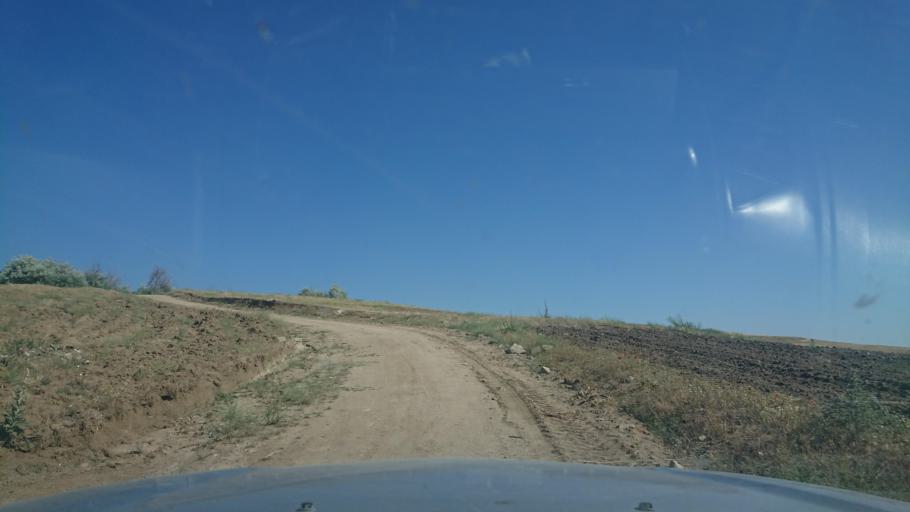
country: TR
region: Aksaray
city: Agacoren
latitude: 38.8451
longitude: 33.9190
